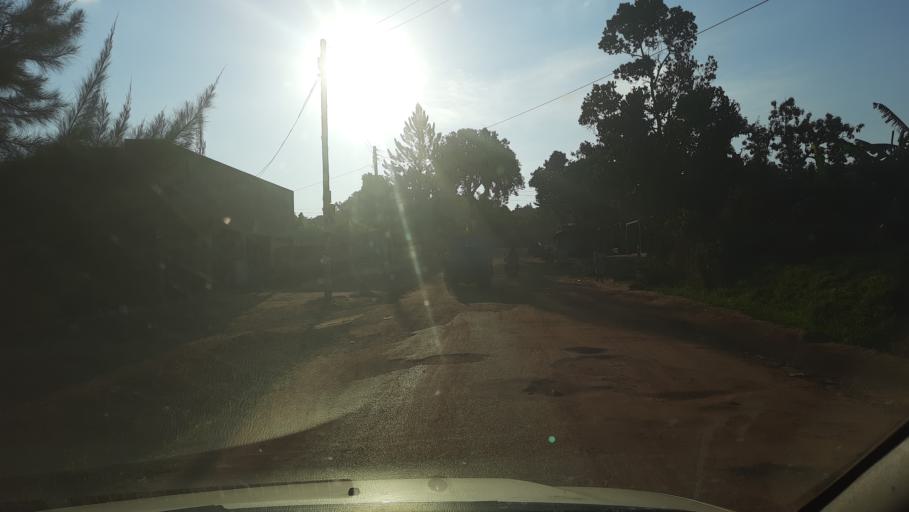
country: UG
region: Central Region
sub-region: Mukono District
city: Mukono
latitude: 0.3710
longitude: 32.7510
